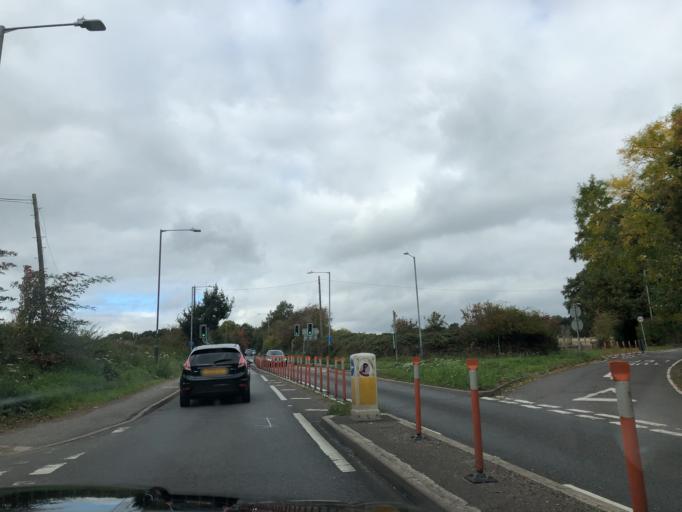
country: GB
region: England
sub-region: Warwickshire
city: Kenilworth
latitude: 52.3268
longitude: -1.5581
